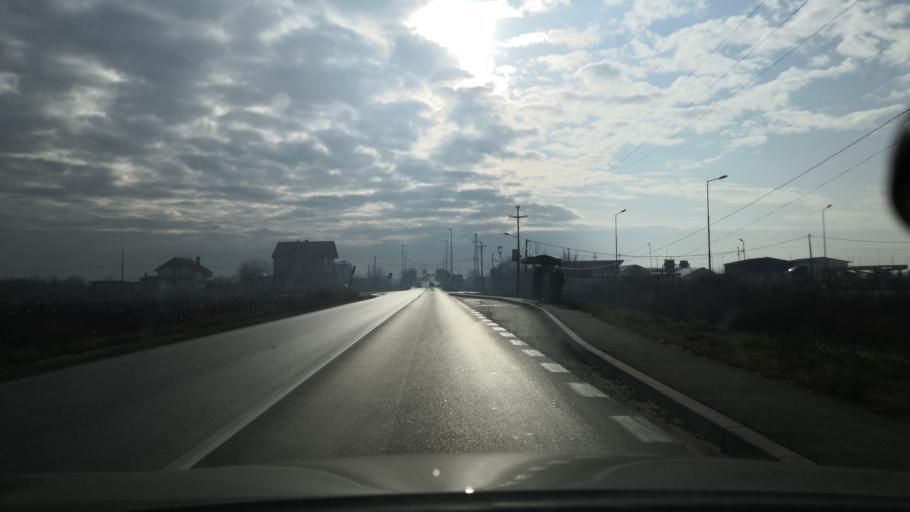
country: RS
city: Dobanovci
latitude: 44.8492
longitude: 20.2082
